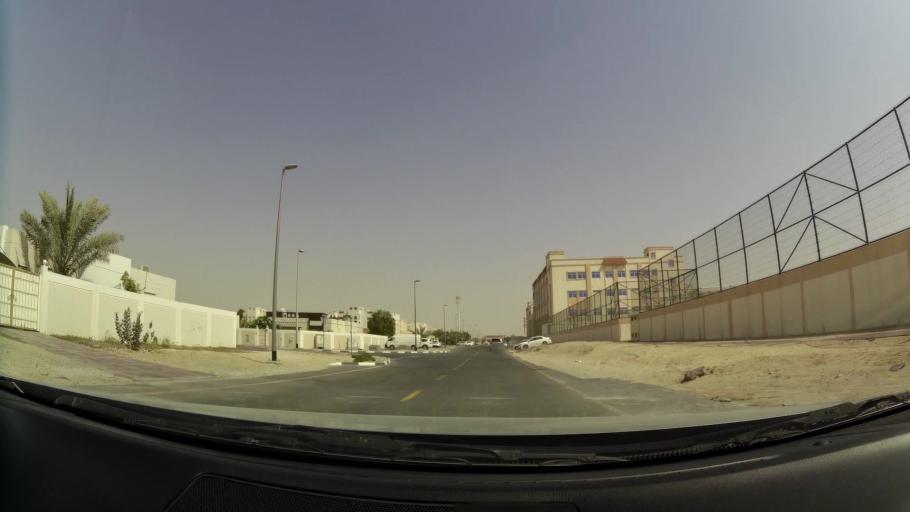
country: AE
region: Dubai
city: Dubai
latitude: 25.1515
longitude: 55.2534
